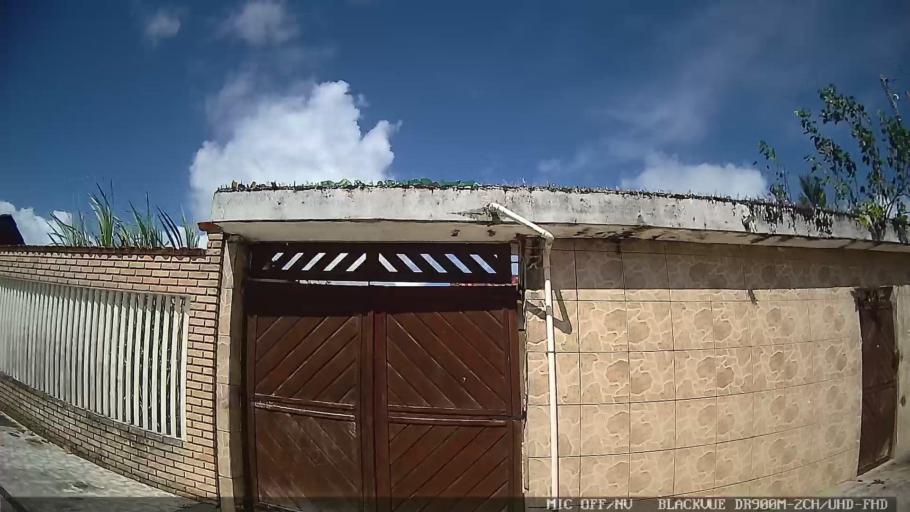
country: BR
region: Sao Paulo
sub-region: Itanhaem
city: Itanhaem
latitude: -24.2383
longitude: -46.8928
